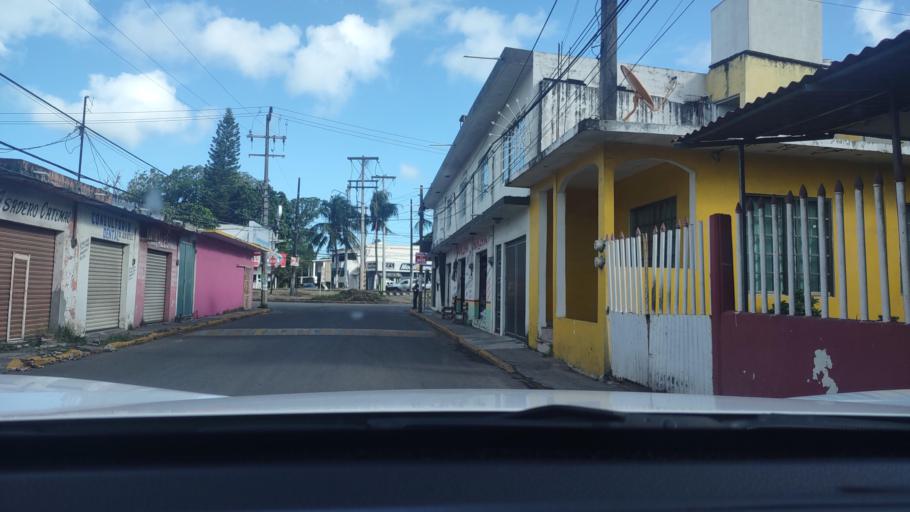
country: MX
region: Veracruz
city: El Tejar
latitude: 19.0741
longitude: -96.1621
